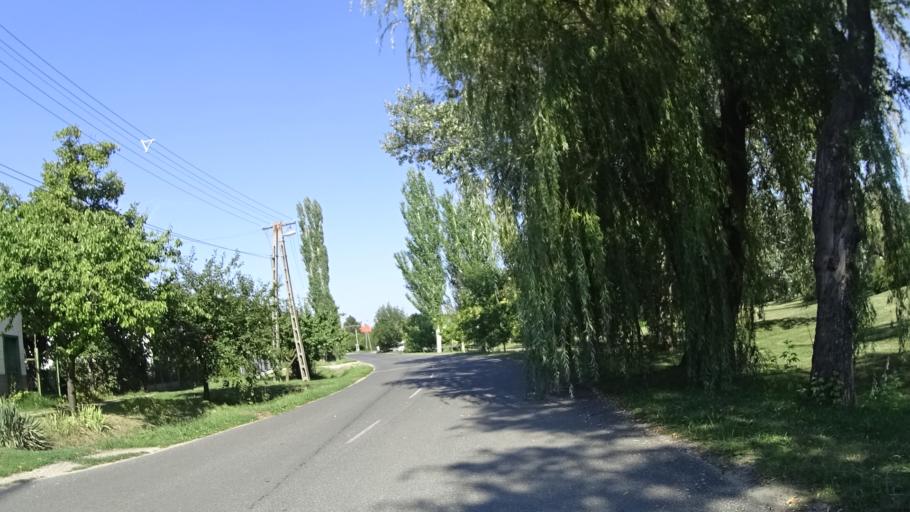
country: HU
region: Fejer
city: Velence
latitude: 47.2373
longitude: 18.6539
